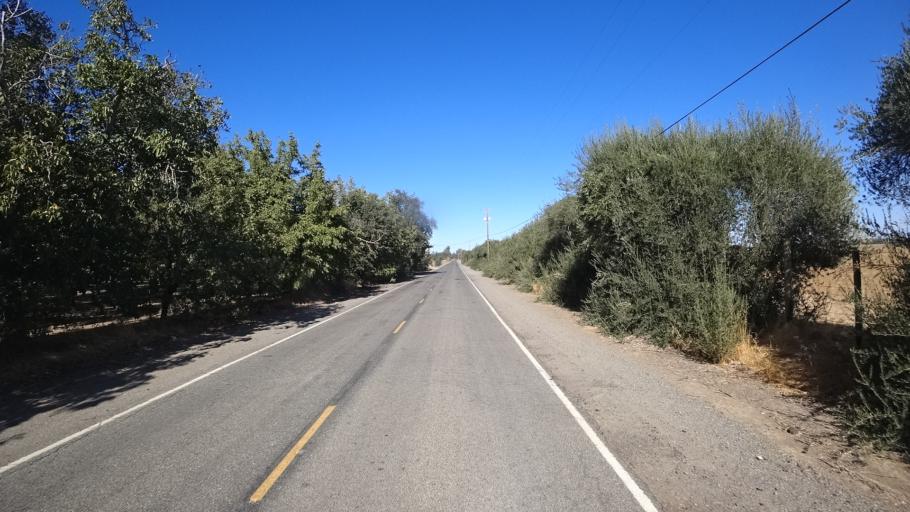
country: US
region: California
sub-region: Solano County
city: Dixon
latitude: 38.5399
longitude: -121.8525
